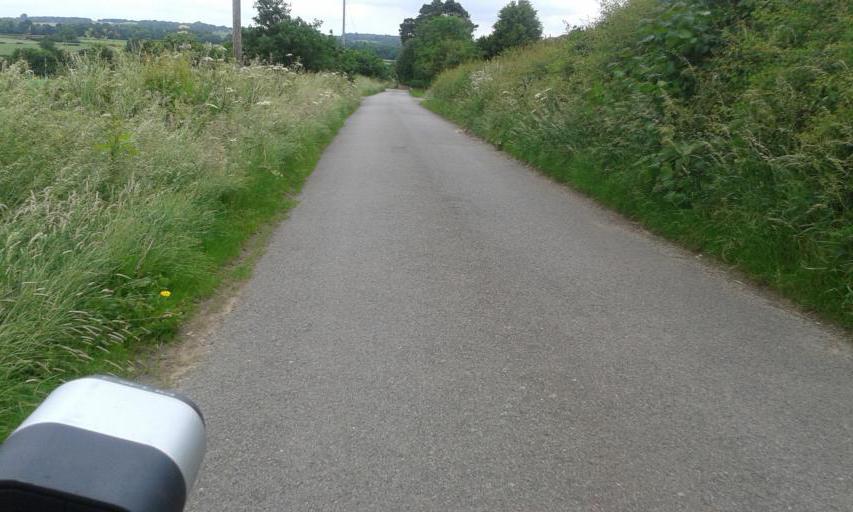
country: GB
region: England
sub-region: Leicestershire
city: Earl Shilton
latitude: 52.5804
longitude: -1.2874
